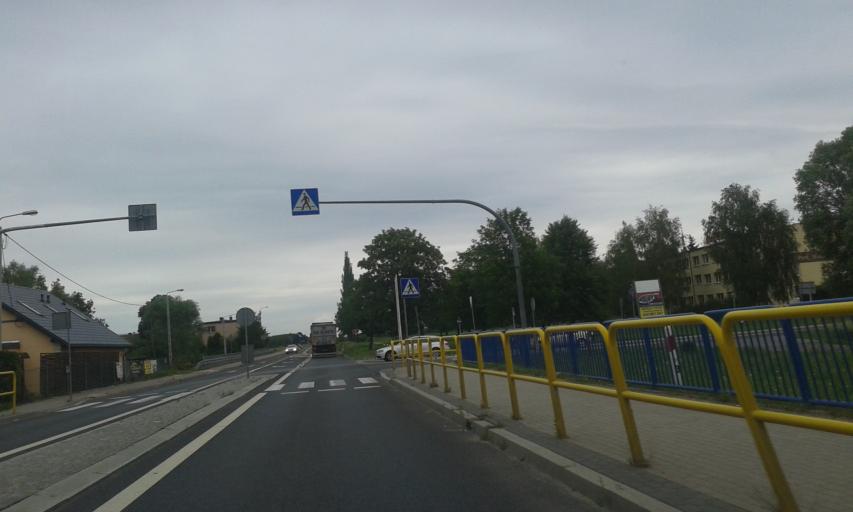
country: PL
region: Kujawsko-Pomorskie
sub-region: Powiat bydgoski
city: Koronowo
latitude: 53.2271
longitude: 17.9182
